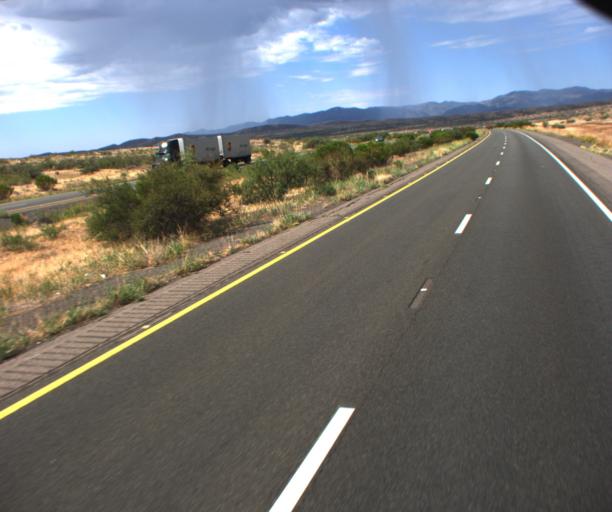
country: US
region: Arizona
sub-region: Yavapai County
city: Spring Valley
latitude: 34.3787
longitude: -112.1020
